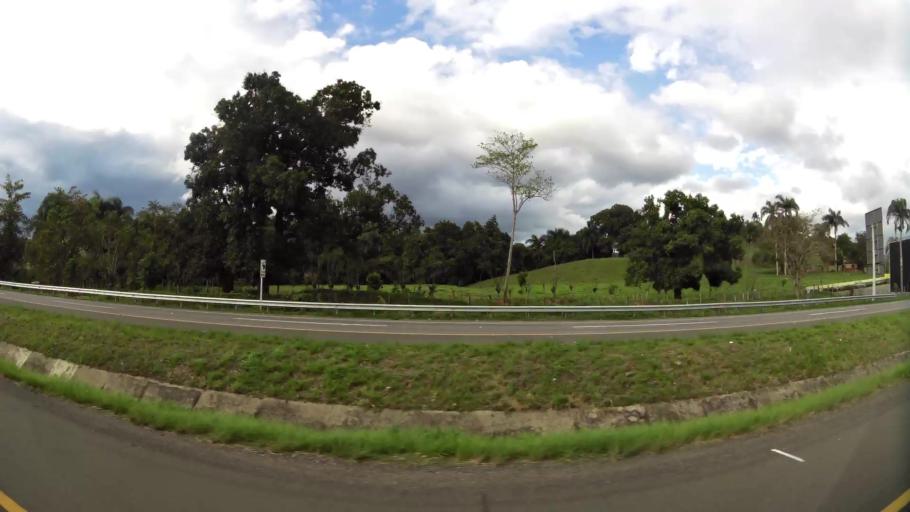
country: DO
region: Monsenor Nouel
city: Piedra Blanca
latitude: 18.8561
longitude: -70.3383
